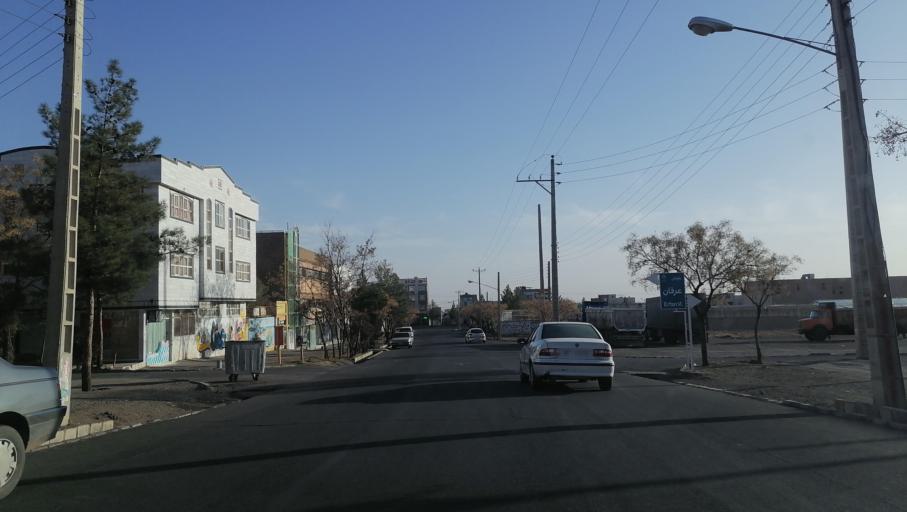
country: IR
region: Razavi Khorasan
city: Sabzevar
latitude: 36.2873
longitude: 57.6764
